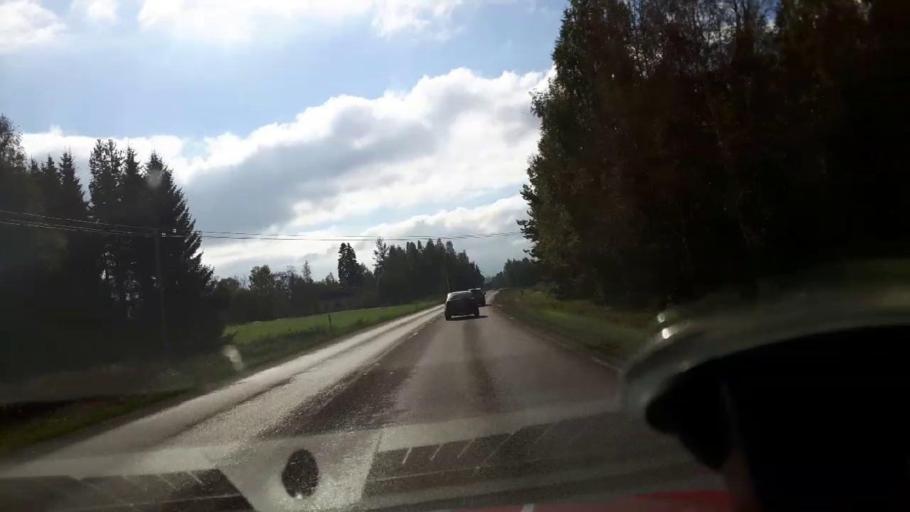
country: SE
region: Gaevleborg
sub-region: Bollnas Kommun
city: Arbra
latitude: 61.5240
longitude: 16.3640
